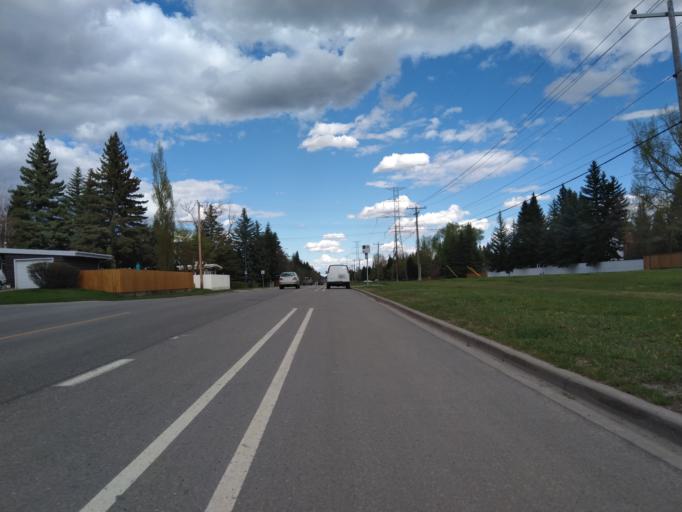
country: CA
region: Alberta
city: Calgary
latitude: 50.9945
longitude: -114.1360
